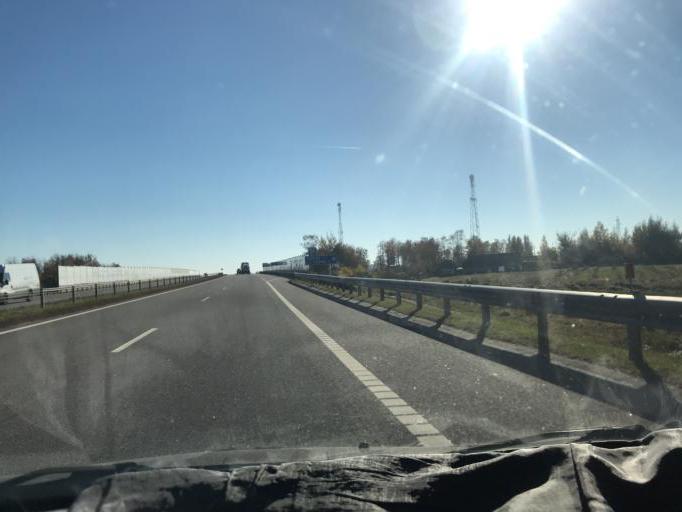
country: BY
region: Mogilev
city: Yalizava
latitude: 53.2497
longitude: 28.9263
